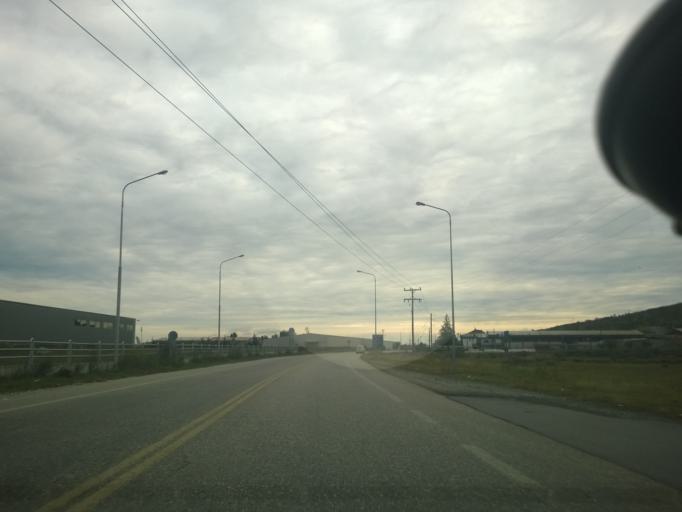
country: GR
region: Central Macedonia
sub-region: Nomos Pellis
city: Mavrovouni
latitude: 40.7984
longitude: 22.1541
